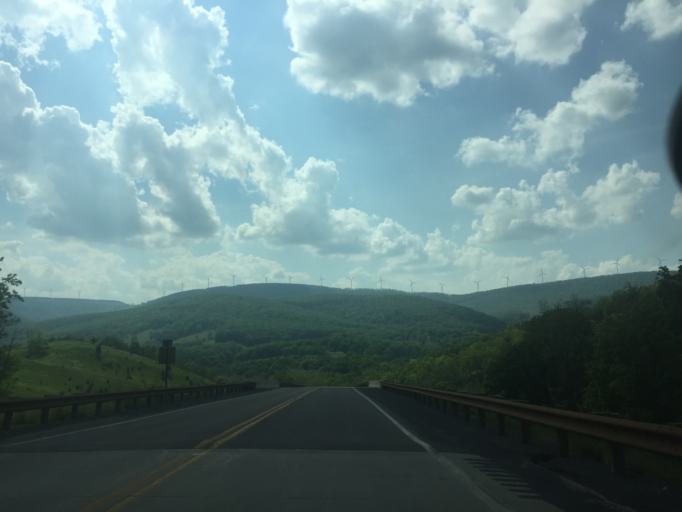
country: US
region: West Virginia
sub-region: Grant County
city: Petersburg
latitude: 39.2191
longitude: -79.1507
